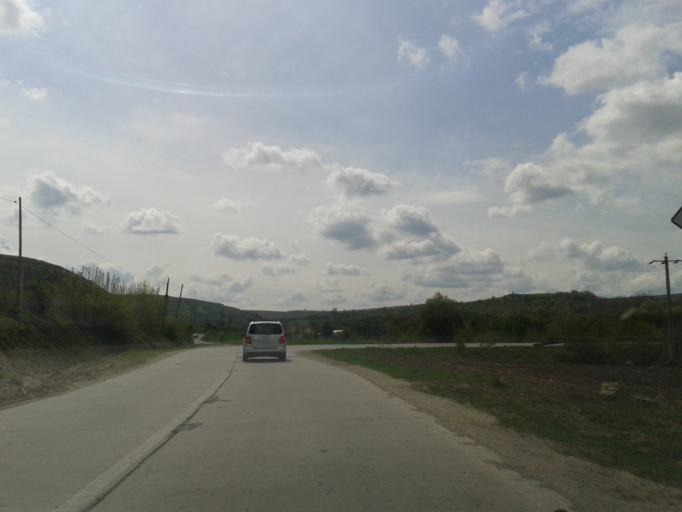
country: RO
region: Sibiu
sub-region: Comuna Micasasa
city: Micasasa
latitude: 46.0771
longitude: 24.1261
